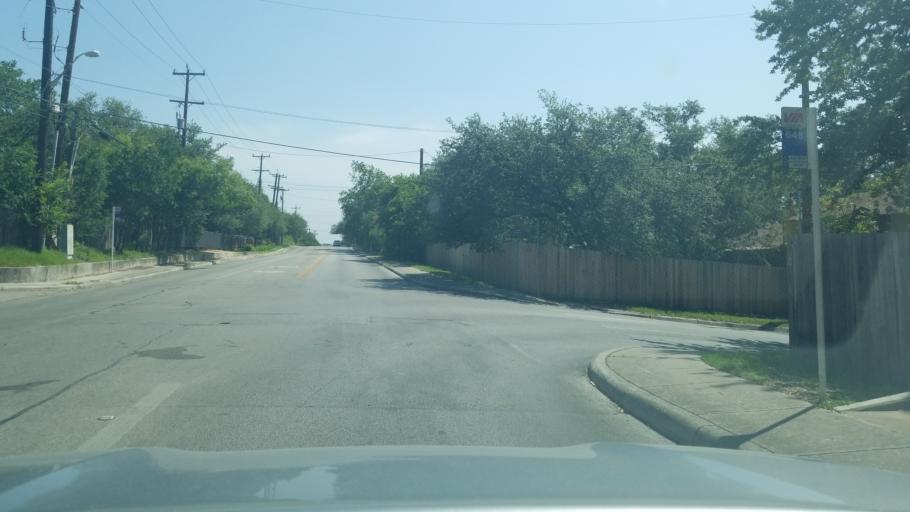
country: US
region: Texas
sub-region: Bexar County
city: Hollywood Park
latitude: 29.5734
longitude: -98.4700
